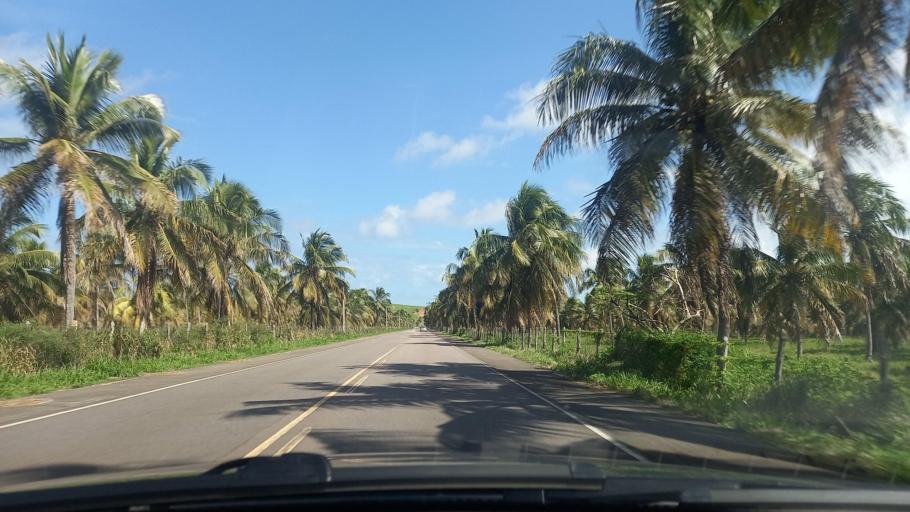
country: BR
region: Alagoas
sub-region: Marechal Deodoro
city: Marechal Deodoro
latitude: -9.8513
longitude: -35.9177
